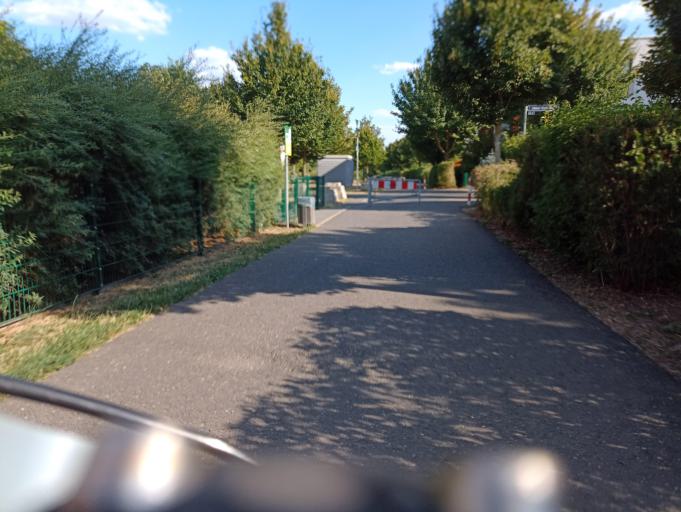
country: DE
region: Hesse
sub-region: Regierungsbezirk Darmstadt
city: Bad Homburg vor der Hoehe
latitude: 50.1827
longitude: 8.6271
